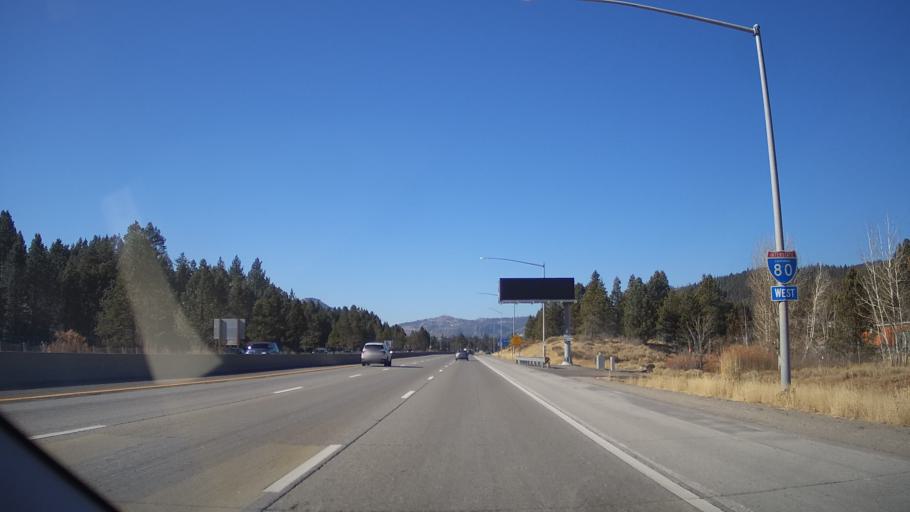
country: US
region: California
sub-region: Nevada County
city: Truckee
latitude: 39.3233
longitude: -120.2113
